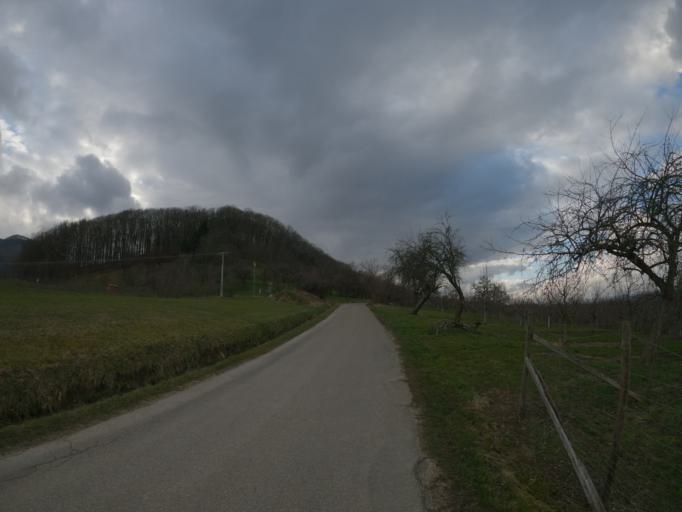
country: DE
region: Baden-Wuerttemberg
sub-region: Regierungsbezirk Stuttgart
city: Schlat
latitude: 48.6526
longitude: 9.6960
